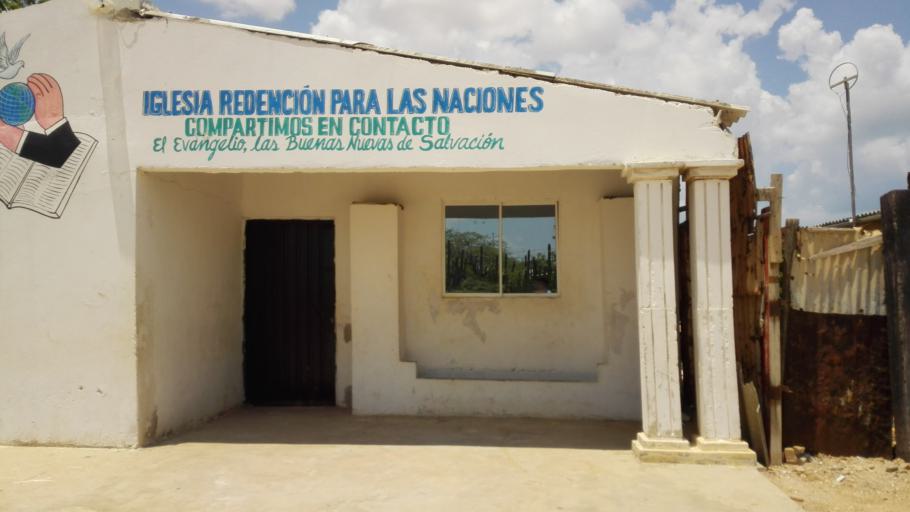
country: CO
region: La Guajira
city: Manaure
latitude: 11.7719
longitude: -72.4449
